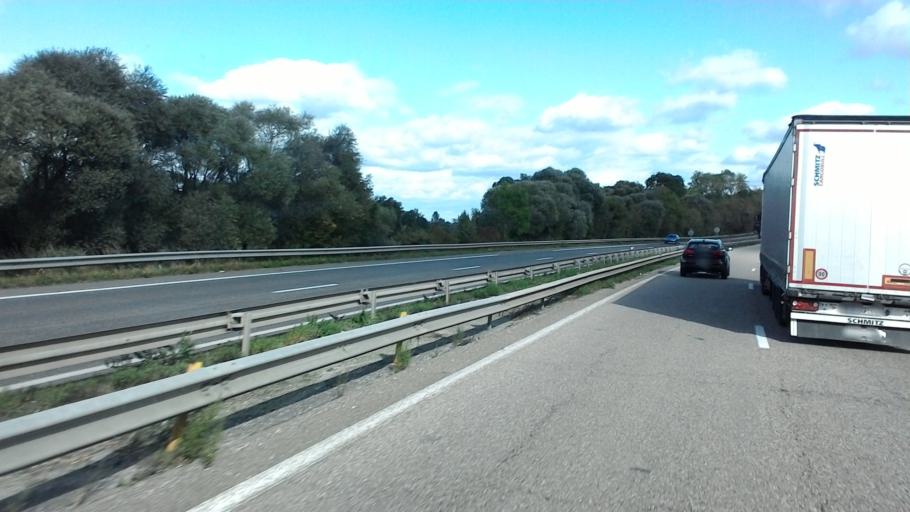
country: FR
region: Lorraine
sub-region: Departement de Meurthe-et-Moselle
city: Dommartin-les-Toul
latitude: 48.6792
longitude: 5.9279
